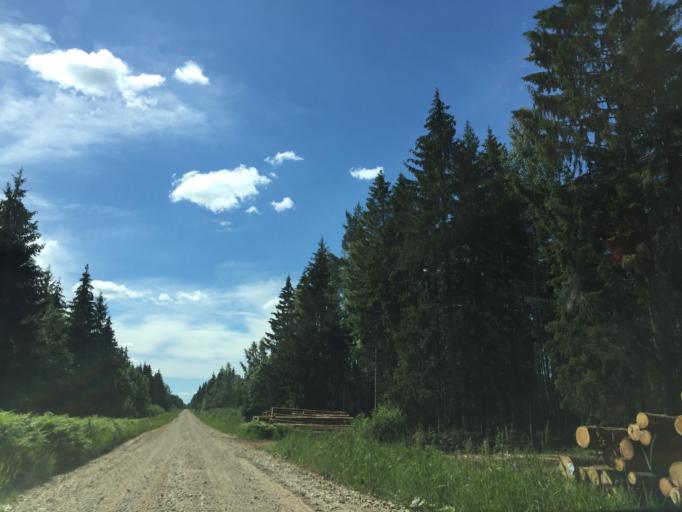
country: LV
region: Ventspils Rajons
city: Piltene
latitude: 57.2753
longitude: 21.8327
